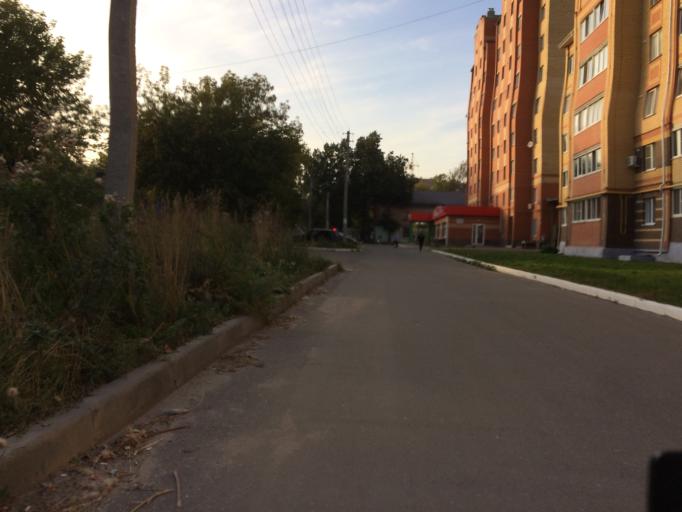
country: RU
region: Mariy-El
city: Medvedevo
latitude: 56.6280
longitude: 47.8478
